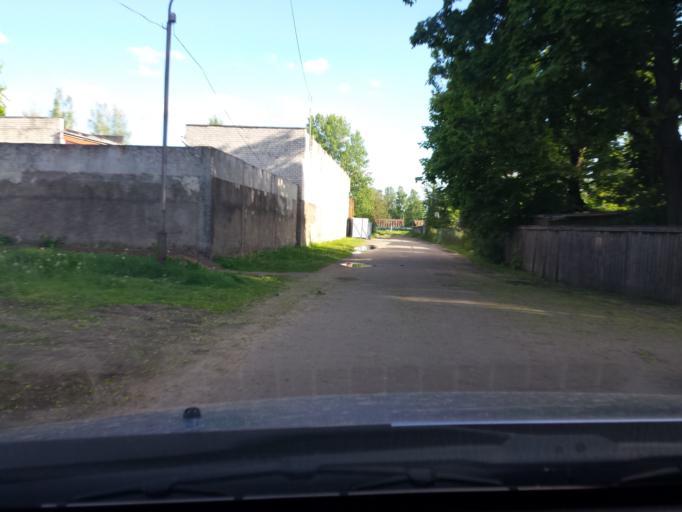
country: LV
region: Riga
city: Jaunciems
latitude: 56.9824
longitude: 24.1675
